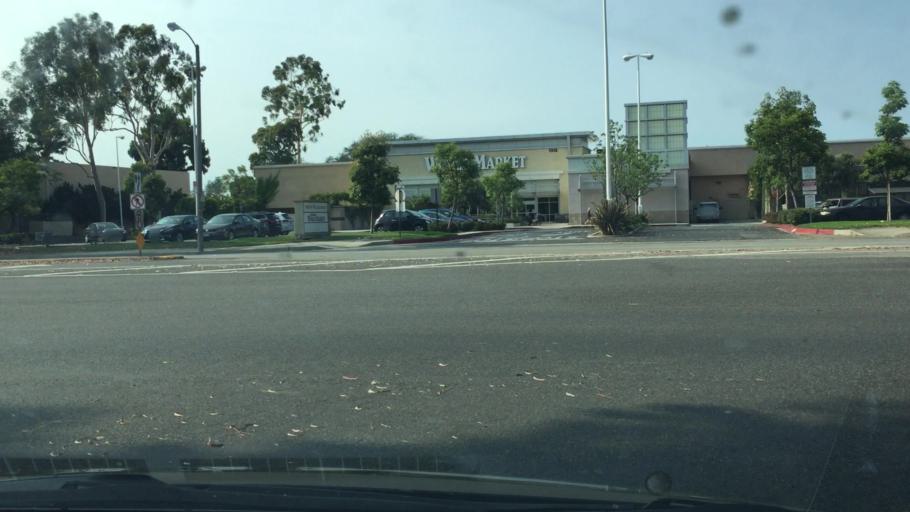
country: US
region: California
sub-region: Orange County
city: Santa Ana
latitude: 33.6940
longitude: -117.8880
